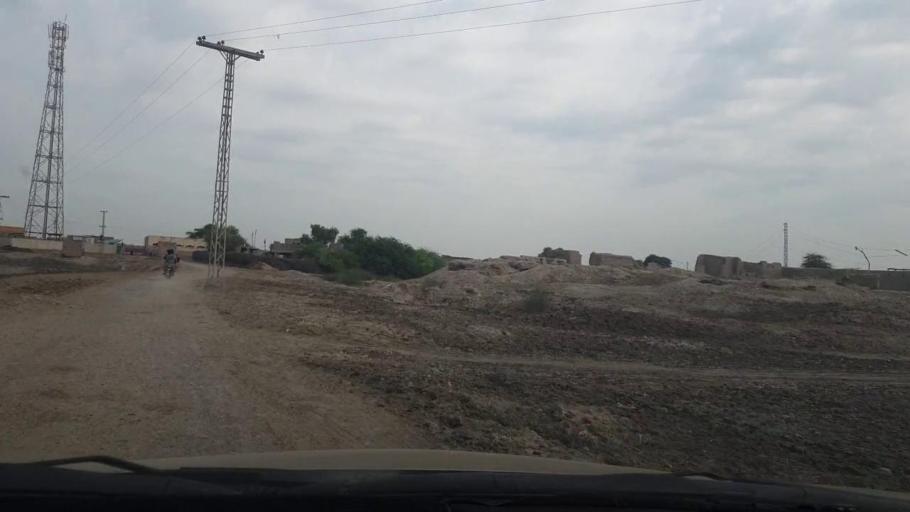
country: PK
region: Sindh
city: Ratodero
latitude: 27.7006
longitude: 68.2298
